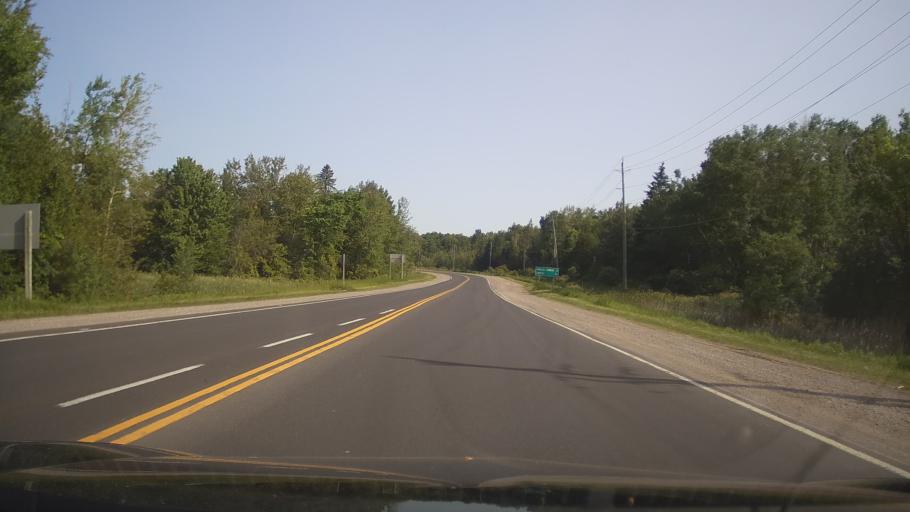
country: CA
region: Ontario
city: Peterborough
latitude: 44.2688
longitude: -78.4089
